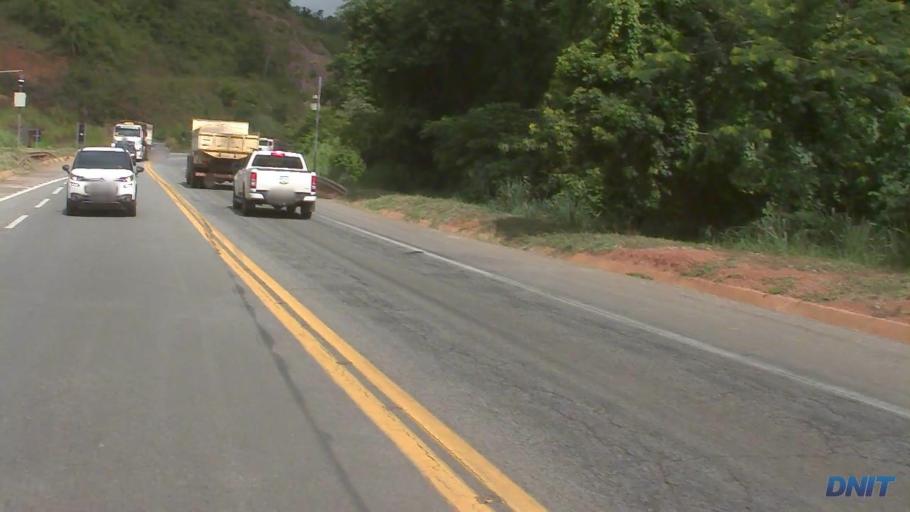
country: BR
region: Minas Gerais
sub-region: Joao Monlevade
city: Joao Monlevade
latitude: -19.8495
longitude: -43.2483
